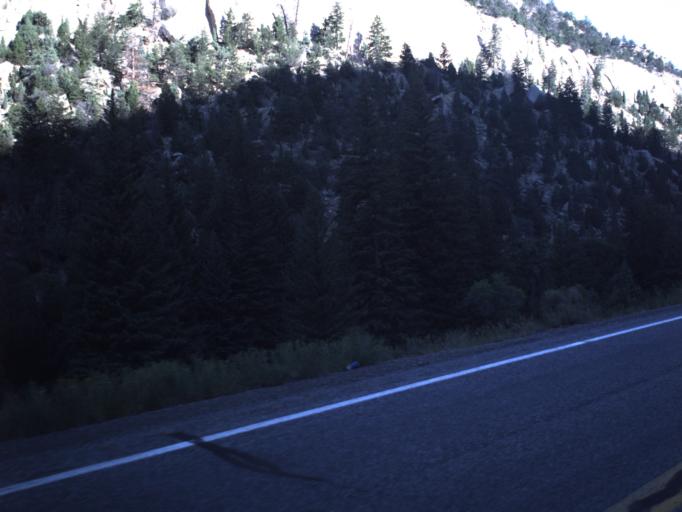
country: US
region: Utah
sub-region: Emery County
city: Huntington
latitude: 39.4271
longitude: -111.1297
